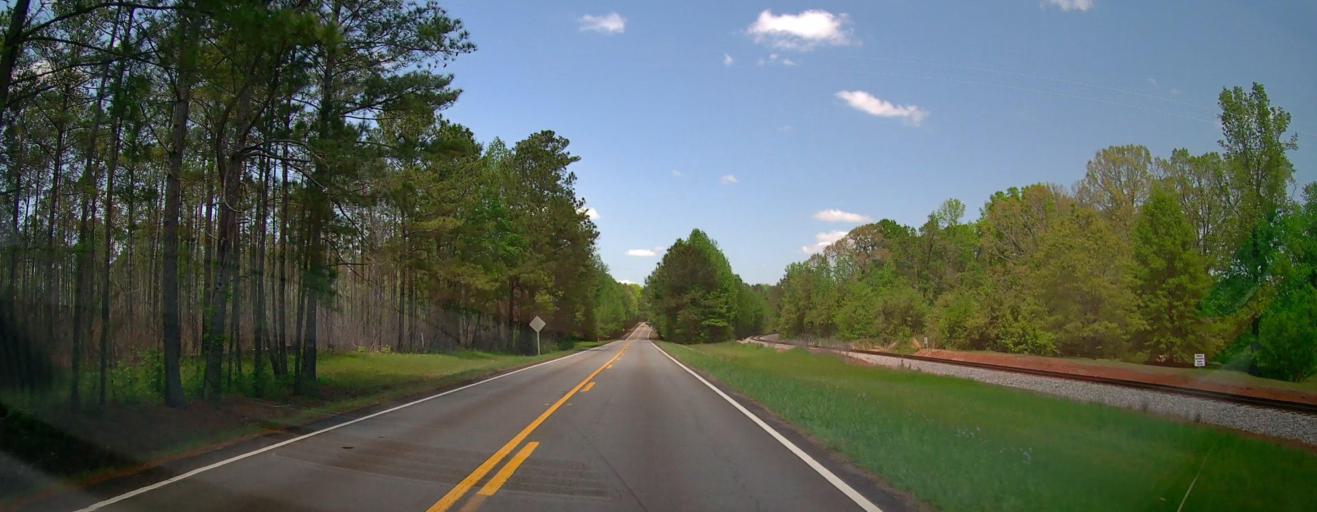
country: US
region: Georgia
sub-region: Jones County
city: Gray
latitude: 33.1217
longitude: -83.6263
